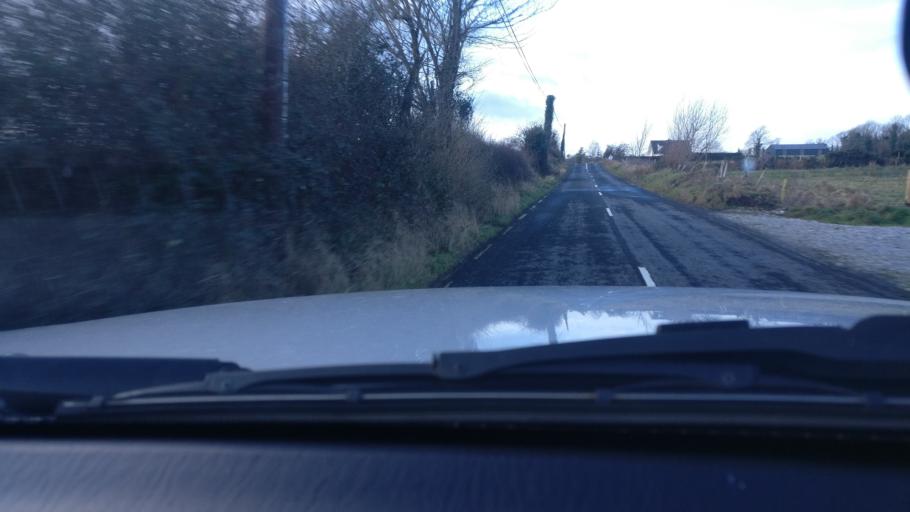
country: IE
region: Connaught
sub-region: County Galway
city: Ballinasloe
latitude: 53.2296
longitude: -8.3303
